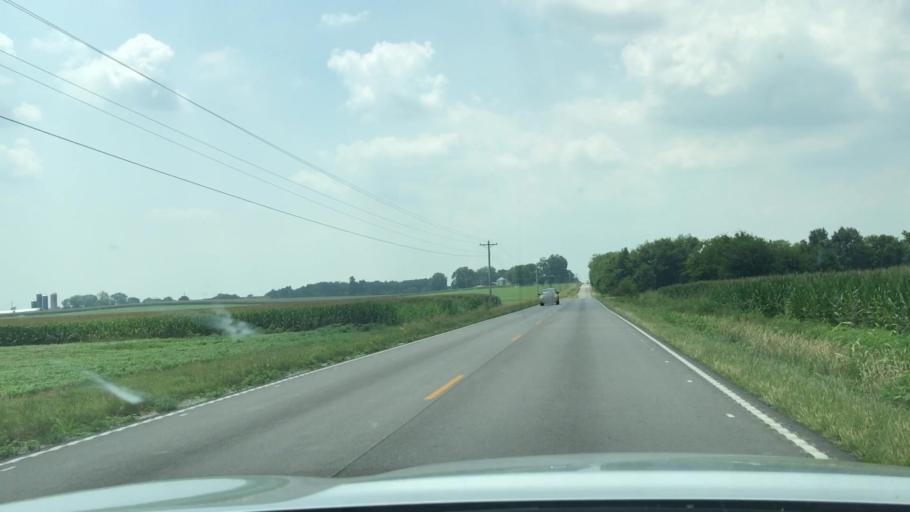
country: US
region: Kentucky
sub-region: Todd County
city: Guthrie
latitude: 36.6828
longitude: -87.1428
